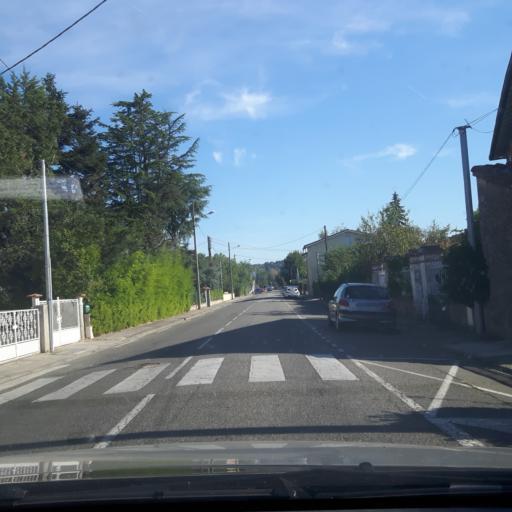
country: FR
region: Midi-Pyrenees
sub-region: Departement de la Haute-Garonne
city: Villemur-sur-Tarn
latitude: 43.8555
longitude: 1.4995
